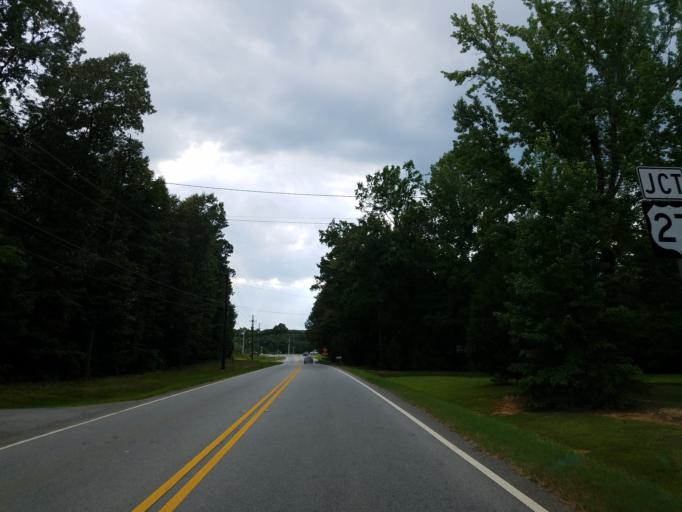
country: US
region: Georgia
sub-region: Floyd County
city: Shannon
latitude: 34.3861
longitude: -85.1750
